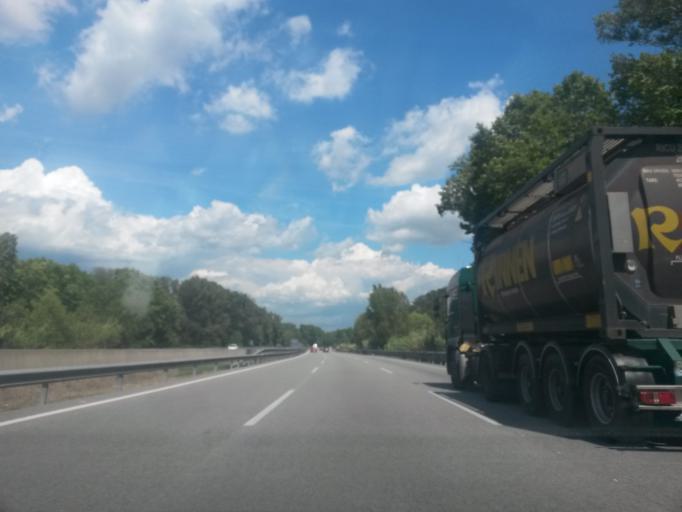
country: ES
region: Catalonia
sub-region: Provincia de Barcelona
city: Sant Celoni
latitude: 41.6864
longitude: 2.5005
